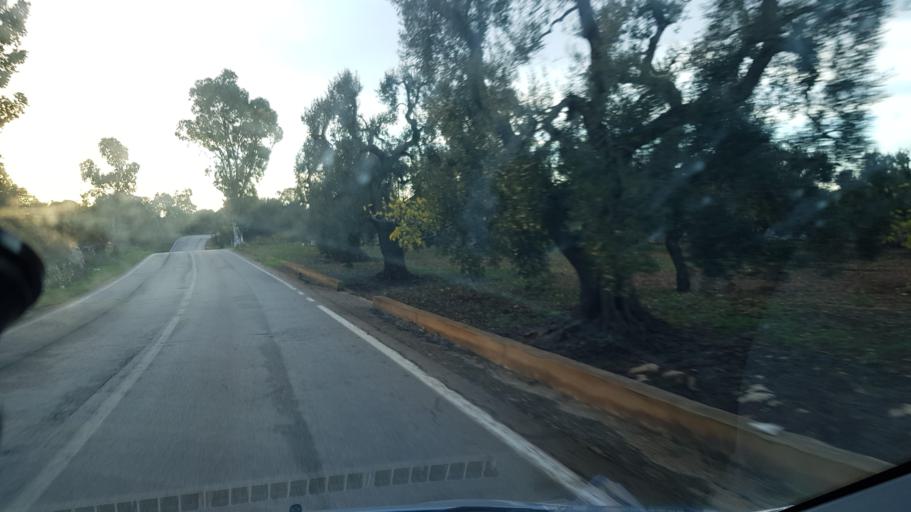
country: IT
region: Apulia
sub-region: Provincia di Brindisi
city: San Michele Salentino
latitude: 40.6416
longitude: 17.5895
